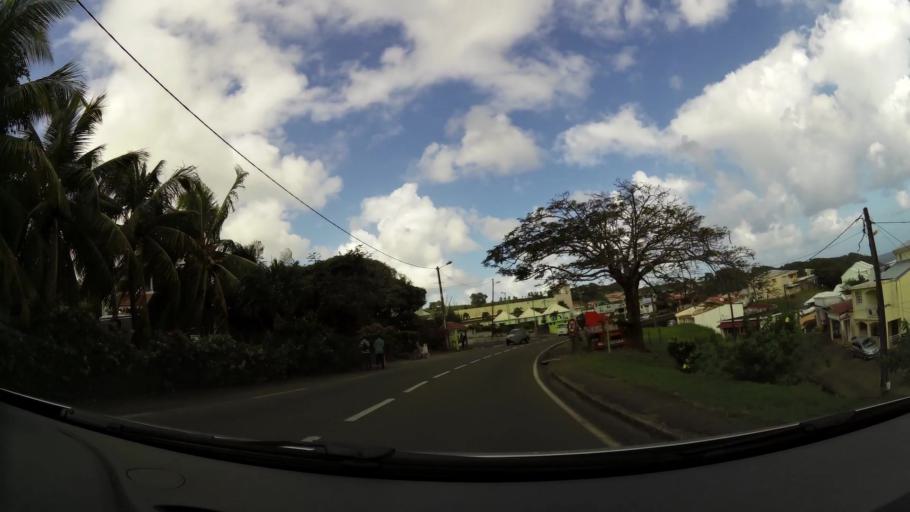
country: MQ
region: Martinique
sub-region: Martinique
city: Le Lorrain
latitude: 14.8208
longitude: -61.0302
